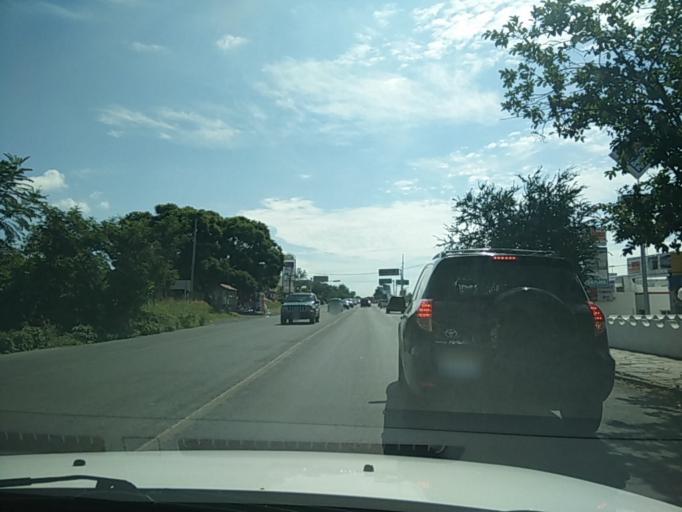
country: MX
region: Jalisco
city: Ajijic
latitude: 20.2981
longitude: -103.2458
